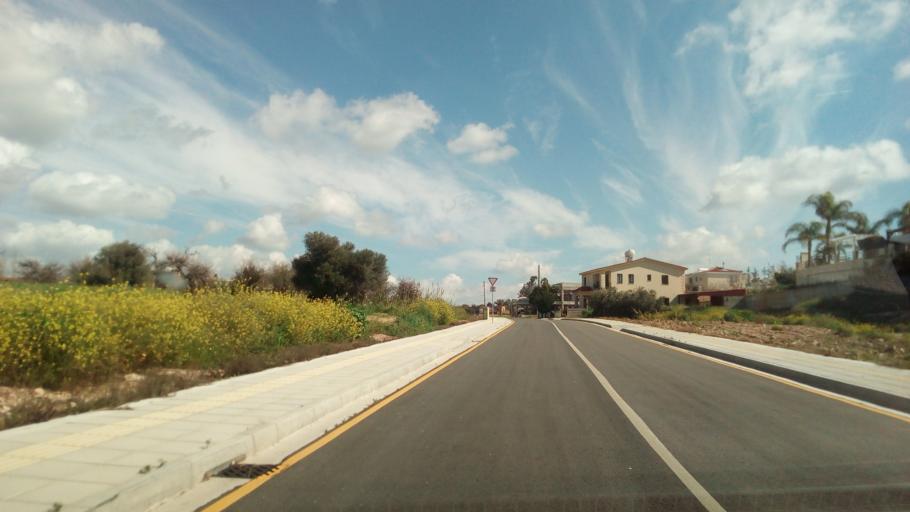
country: CY
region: Pafos
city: Mesogi
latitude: 34.7395
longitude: 32.5353
